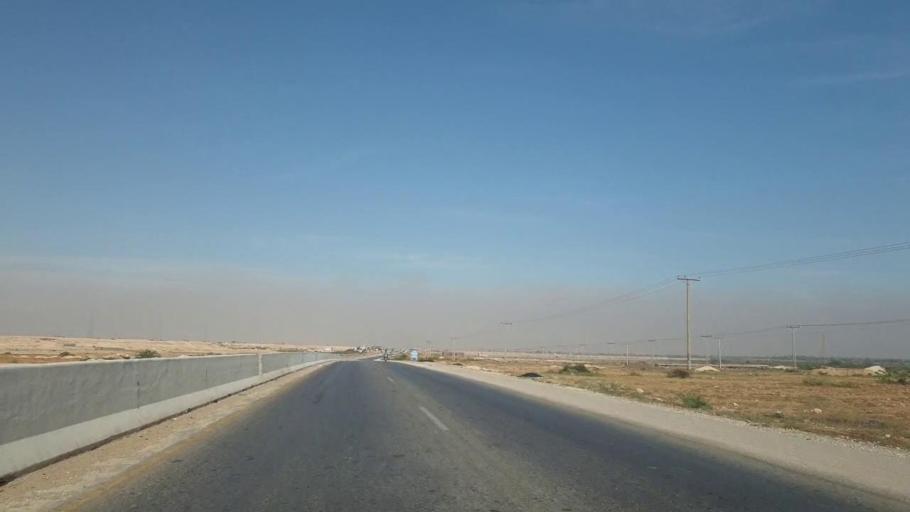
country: PK
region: Sindh
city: Jamshoro
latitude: 25.4887
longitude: 68.2720
